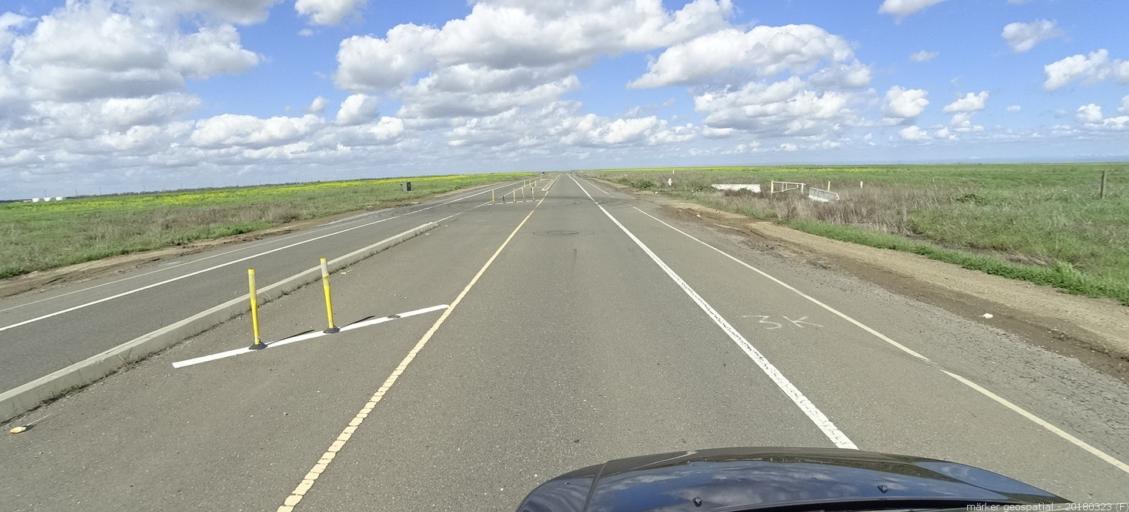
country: US
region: California
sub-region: Sacramento County
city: Elverta
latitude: 38.6881
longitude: -121.5696
